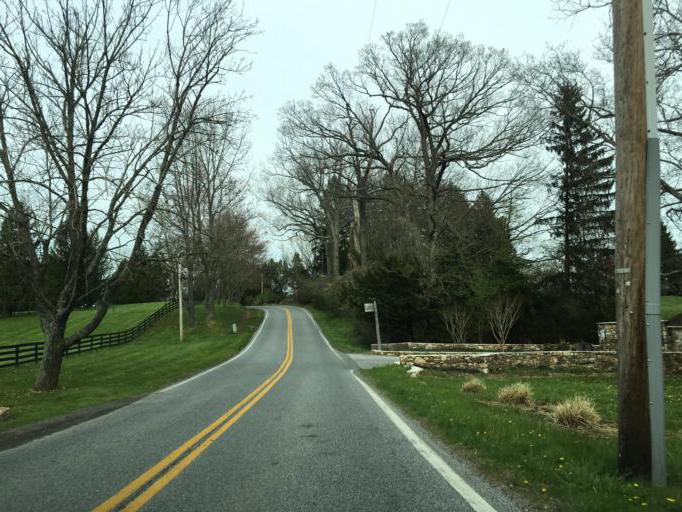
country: US
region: Maryland
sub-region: Baltimore County
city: Hunt Valley
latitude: 39.5508
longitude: -76.6048
